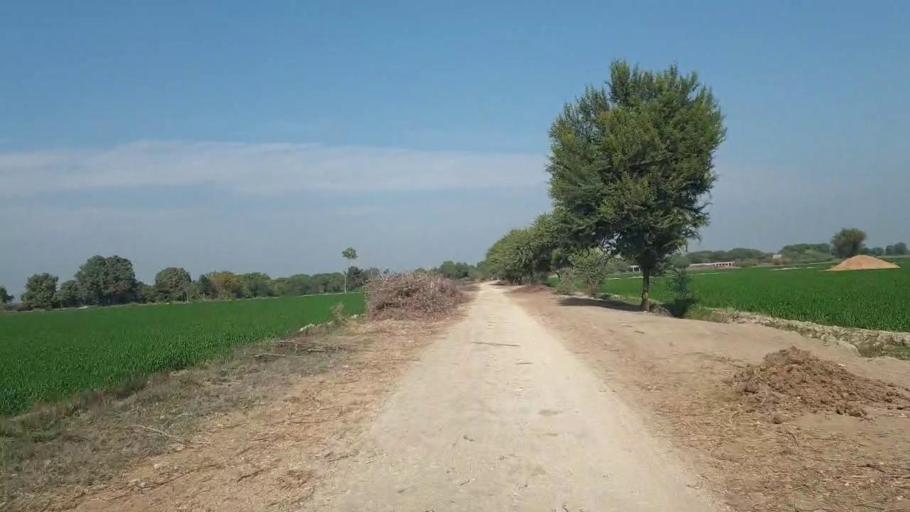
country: PK
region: Sindh
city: Shahdadpur
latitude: 25.9874
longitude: 68.5302
